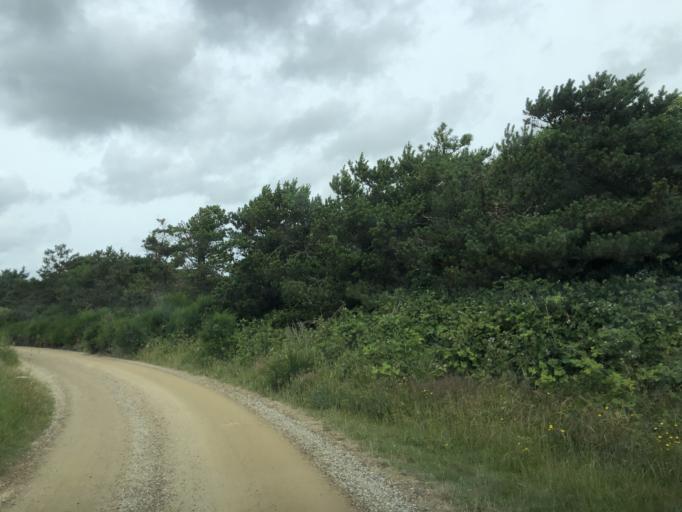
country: DK
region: Central Jutland
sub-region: Ringkobing-Skjern Kommune
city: Hvide Sande
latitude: 55.9231
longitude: 8.1702
